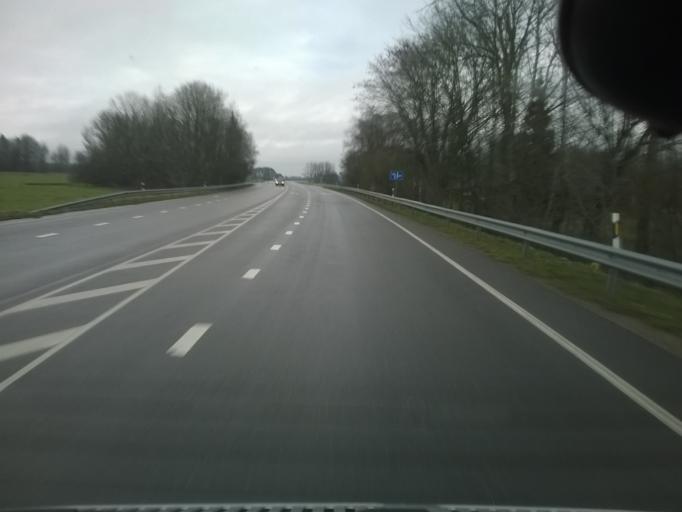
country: EE
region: Laeaene
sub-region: Ridala Parish
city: Uuemoisa
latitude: 58.9563
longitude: 23.7793
